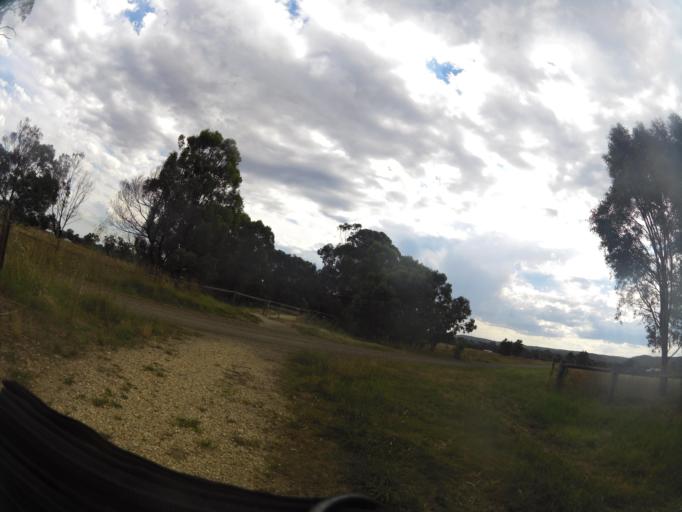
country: AU
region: Victoria
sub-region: Wellington
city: Heyfield
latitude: -38.0500
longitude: 146.6315
